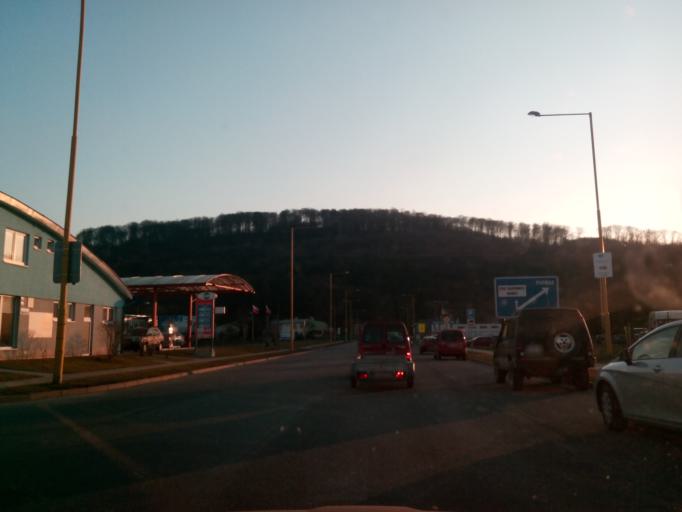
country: SK
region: Presovsky
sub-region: Okres Presov
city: Presov
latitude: 48.9844
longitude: 21.2367
